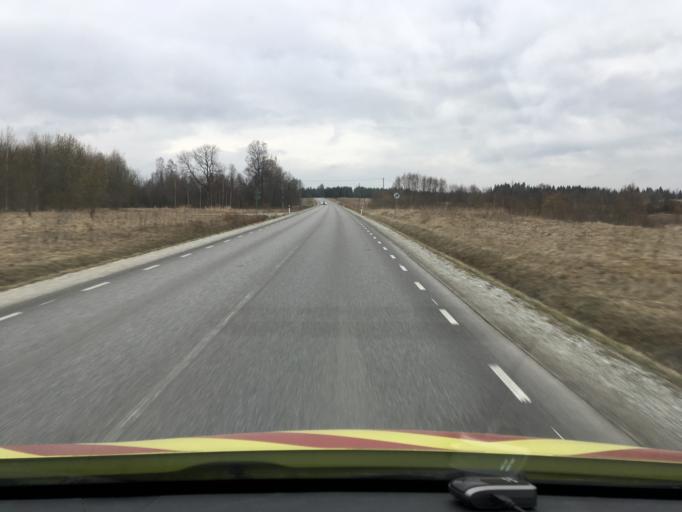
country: EE
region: Raplamaa
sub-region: Rapla vald
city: Rapla
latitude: 59.0006
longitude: 24.8426
